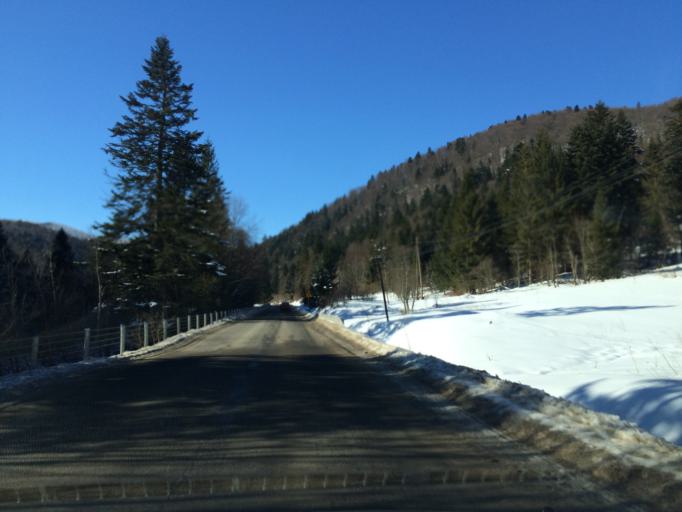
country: PL
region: Subcarpathian Voivodeship
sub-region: Powiat leski
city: Cisna
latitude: 49.2079
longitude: 22.3158
